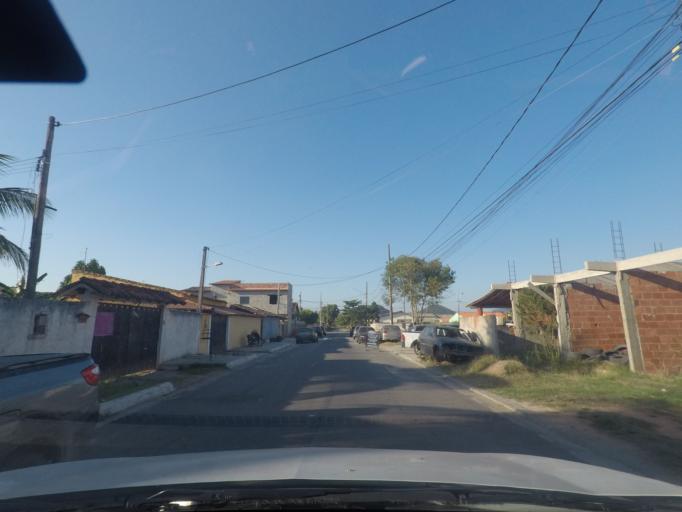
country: BR
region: Rio de Janeiro
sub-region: Marica
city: Marica
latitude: -22.9573
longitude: -42.9371
